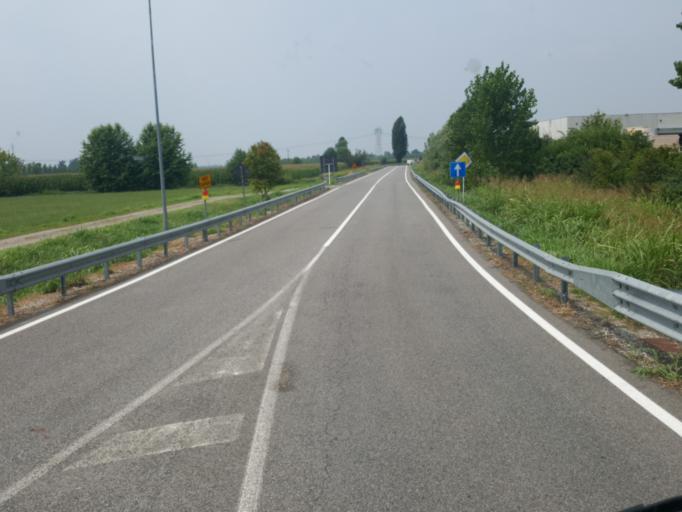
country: IT
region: Lombardy
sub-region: Provincia di Cremona
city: Pandino
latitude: 45.3940
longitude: 9.5477
